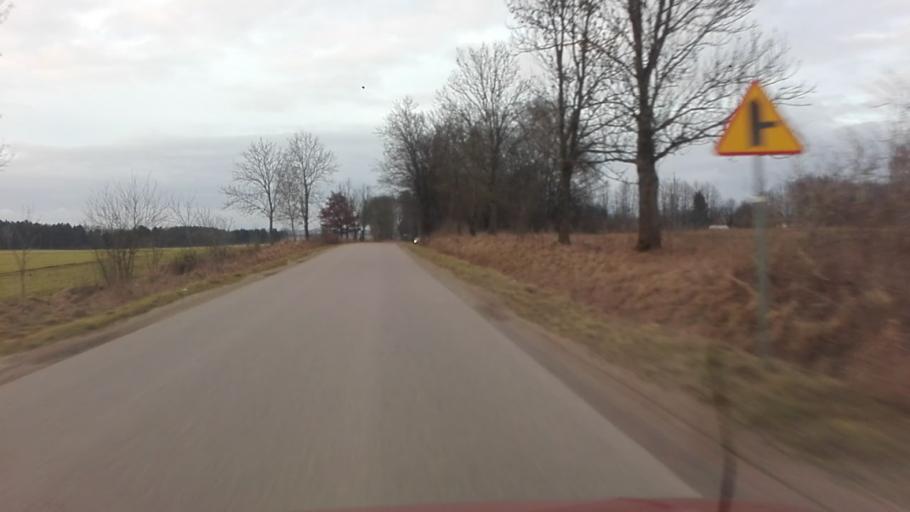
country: PL
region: West Pomeranian Voivodeship
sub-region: Powiat swidwinski
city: Rabino
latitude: 53.7942
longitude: 15.9061
